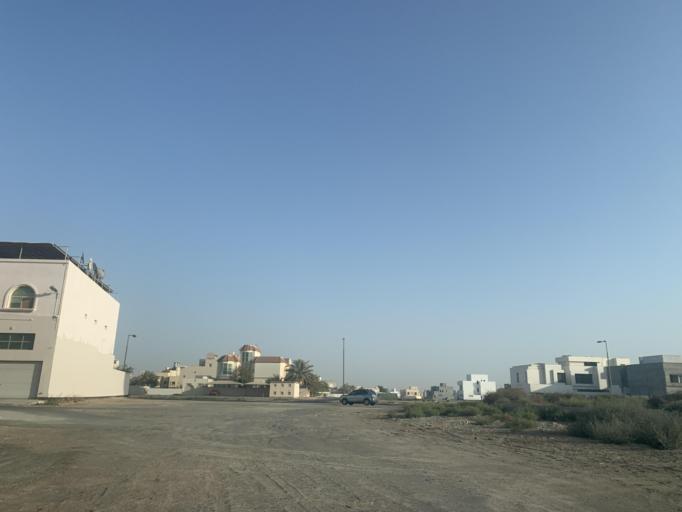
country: BH
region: Manama
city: Jidd Hafs
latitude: 26.2085
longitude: 50.5277
